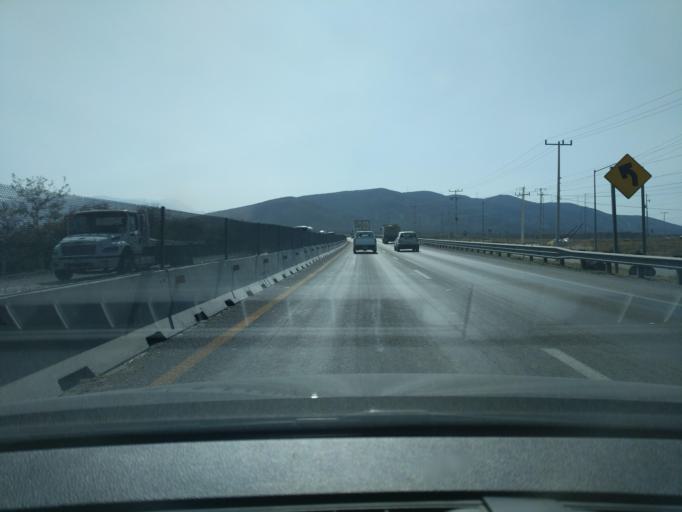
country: MX
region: Nuevo Leon
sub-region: Garcia
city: Los Parques
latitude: 25.7664
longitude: -100.4882
